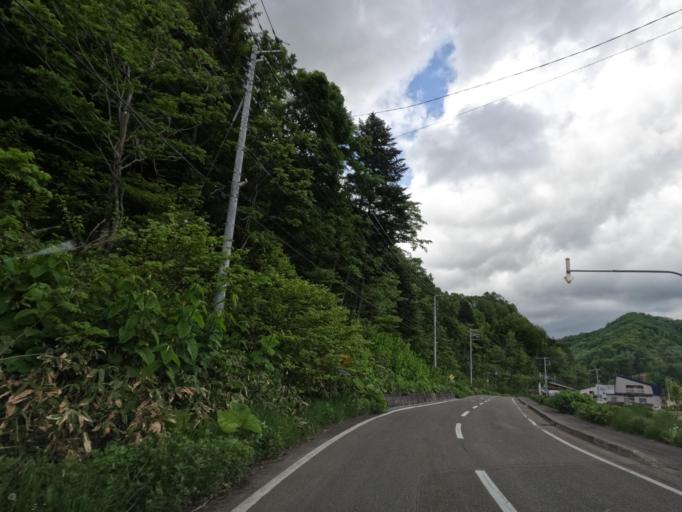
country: JP
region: Hokkaido
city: Takikawa
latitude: 43.5920
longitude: 141.7305
